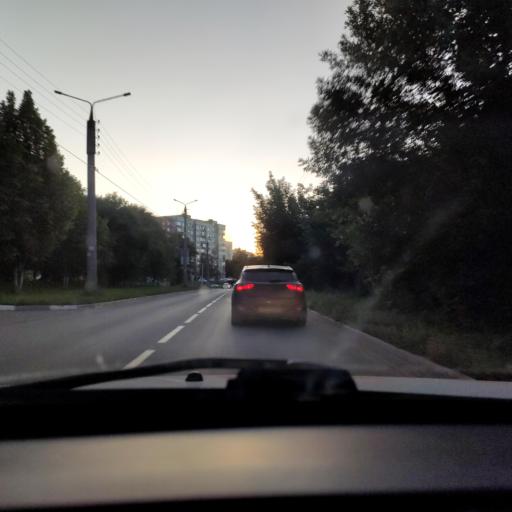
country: RU
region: Samara
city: Novokuybyshevsk
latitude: 53.0969
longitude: 49.9847
